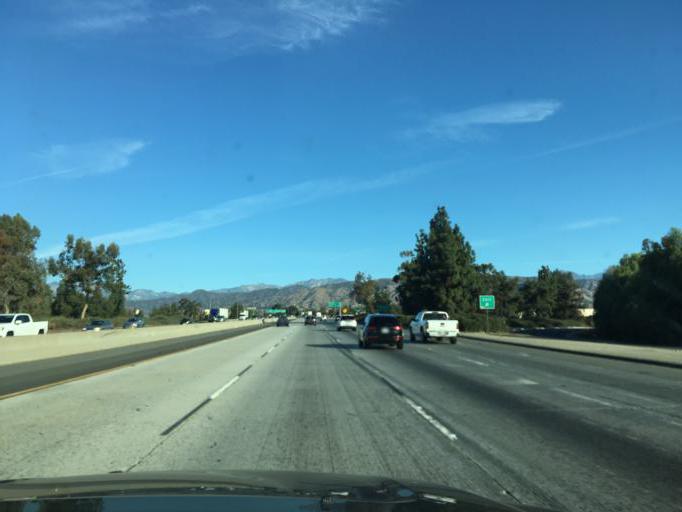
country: US
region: California
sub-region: Los Angeles County
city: San Dimas
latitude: 34.0966
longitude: -117.8194
